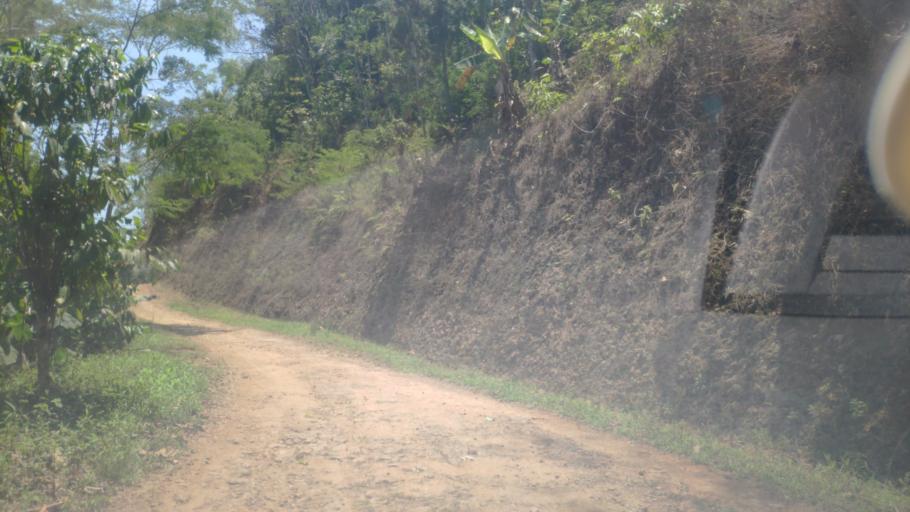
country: ID
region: Central Java
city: Buaran
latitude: -7.2802
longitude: 109.5877
